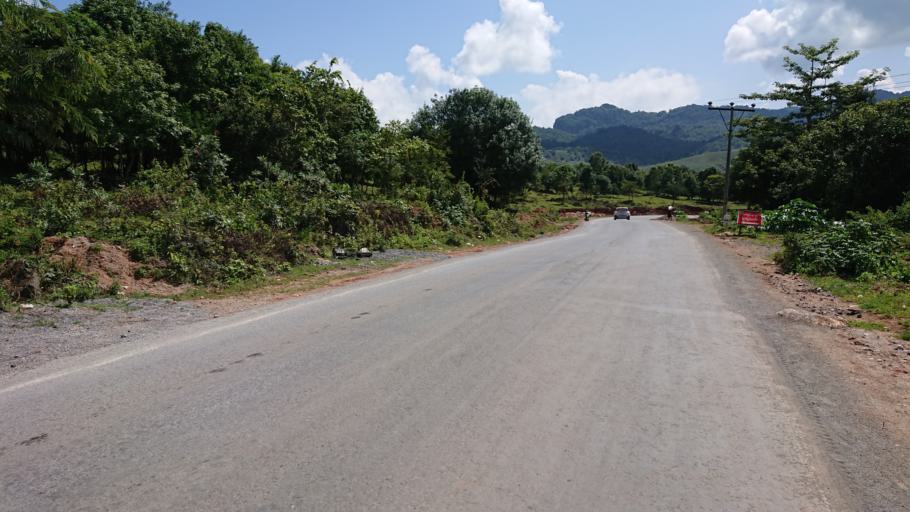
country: MM
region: Shan
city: Taunggyi
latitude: 20.8153
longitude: 97.3274
